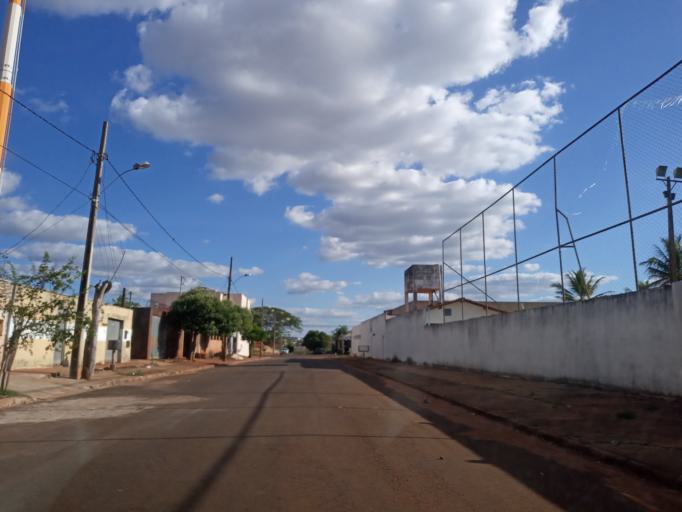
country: BR
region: Minas Gerais
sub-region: Ituiutaba
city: Ituiutaba
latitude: -18.9711
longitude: -49.4430
